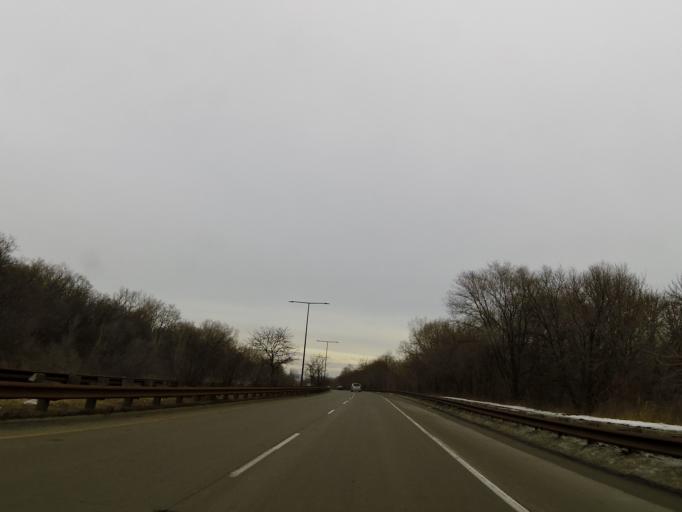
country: US
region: Minnesota
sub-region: Dakota County
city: Mendota Heights
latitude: 44.9136
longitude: -93.1379
